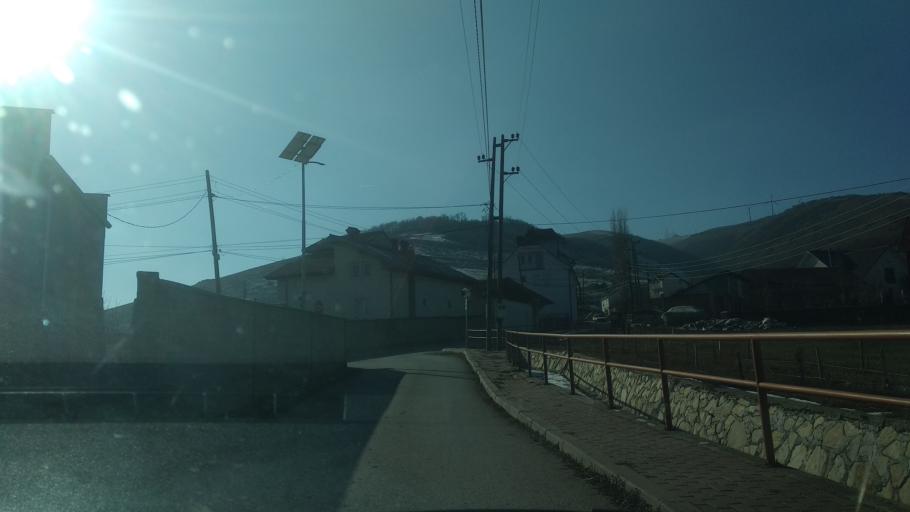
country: XK
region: Pristina
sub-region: Komuna e Gracanices
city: Glanica
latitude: 42.5846
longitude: 21.0031
